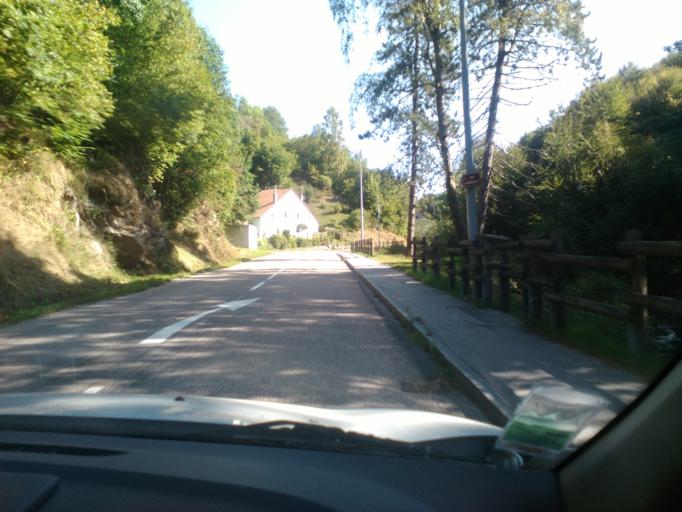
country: FR
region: Lorraine
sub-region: Departement des Vosges
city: La Bresse
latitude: 48.0114
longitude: 6.8862
